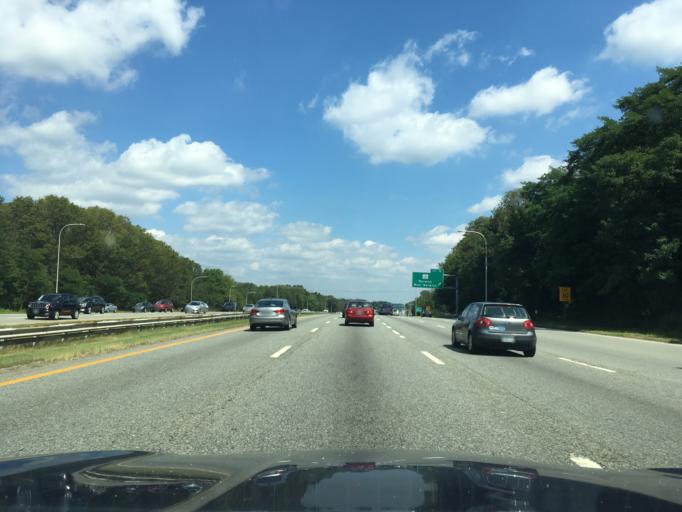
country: US
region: Rhode Island
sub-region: Kent County
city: East Greenwich
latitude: 41.6918
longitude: -71.4769
